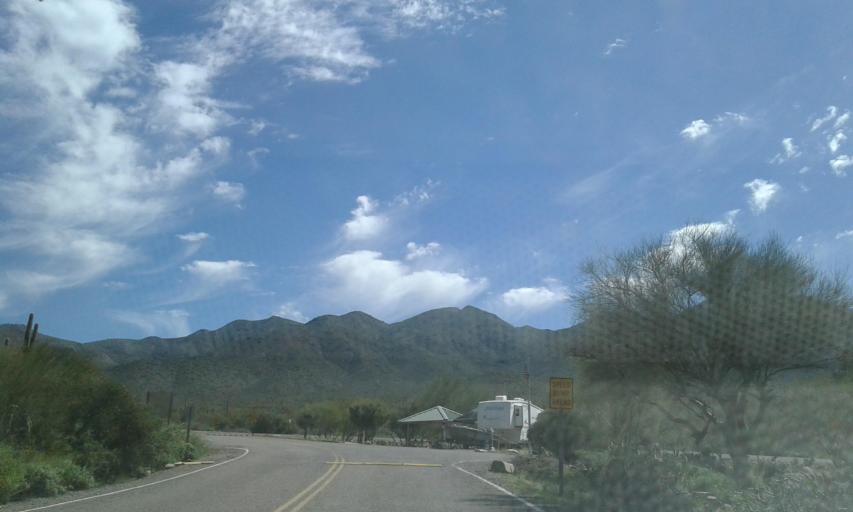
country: US
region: Arizona
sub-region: Gila County
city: Tonto Basin
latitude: 33.6250
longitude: -111.2021
